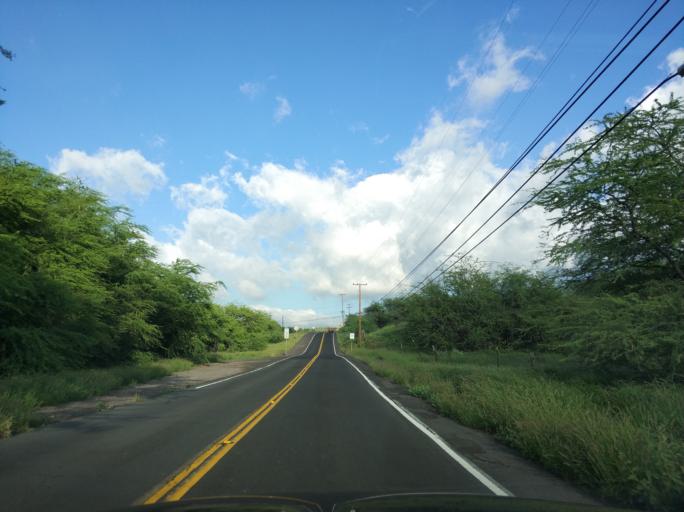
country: US
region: Hawaii
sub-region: Hawaii County
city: Waikoloa Village
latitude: 19.9738
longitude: -155.8297
